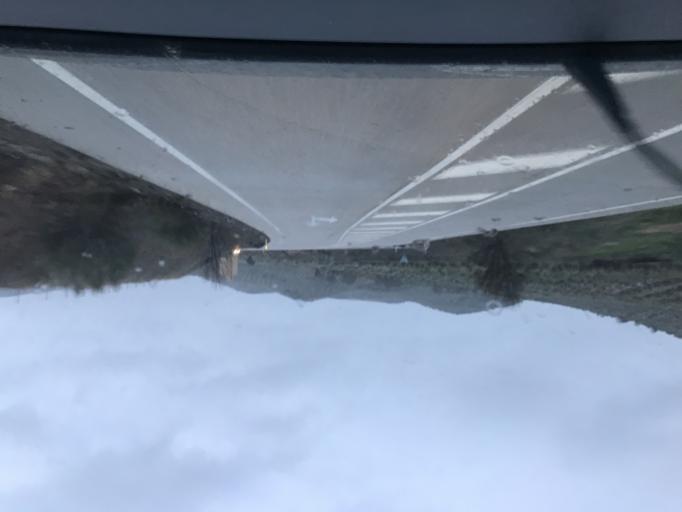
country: ES
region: Andalusia
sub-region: Provincia de Granada
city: Campotejar
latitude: 37.4528
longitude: -3.6363
